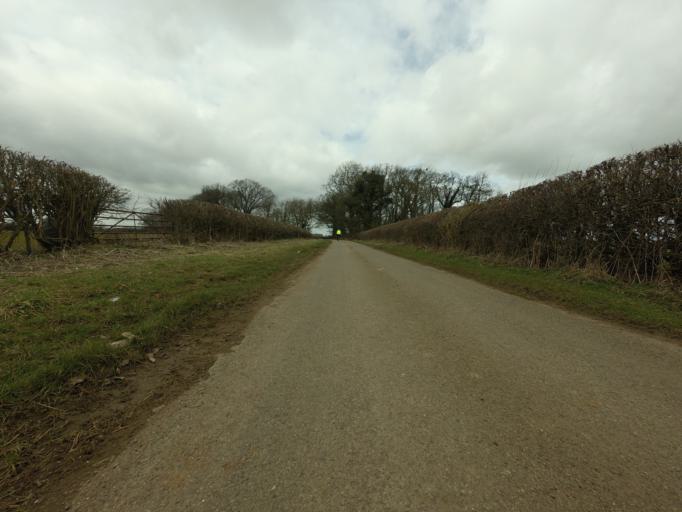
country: GB
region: England
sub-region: Lincolnshire
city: Barrowby
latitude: 52.8700
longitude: -0.6826
